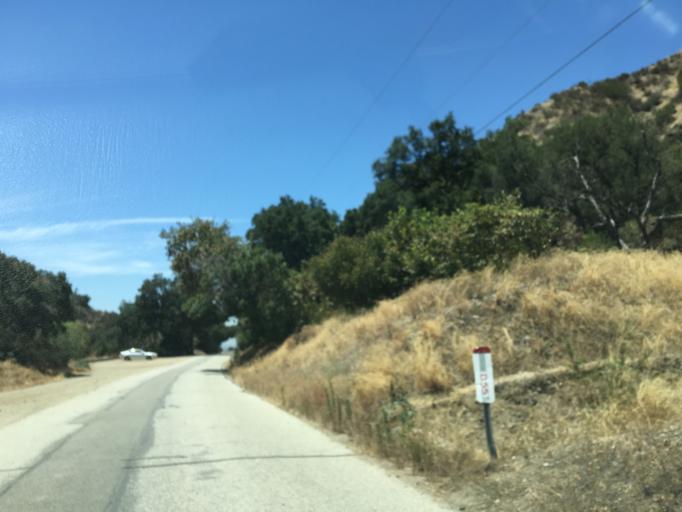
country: US
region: California
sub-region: Los Angeles County
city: Glendora
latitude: 34.1591
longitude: -117.8279
